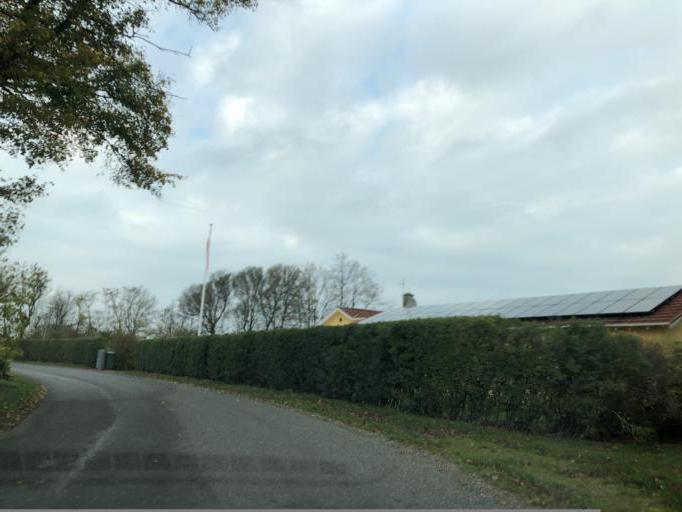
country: DK
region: Central Jutland
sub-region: Hedensted Kommune
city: Hornsyld
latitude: 55.7454
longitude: 9.8074
